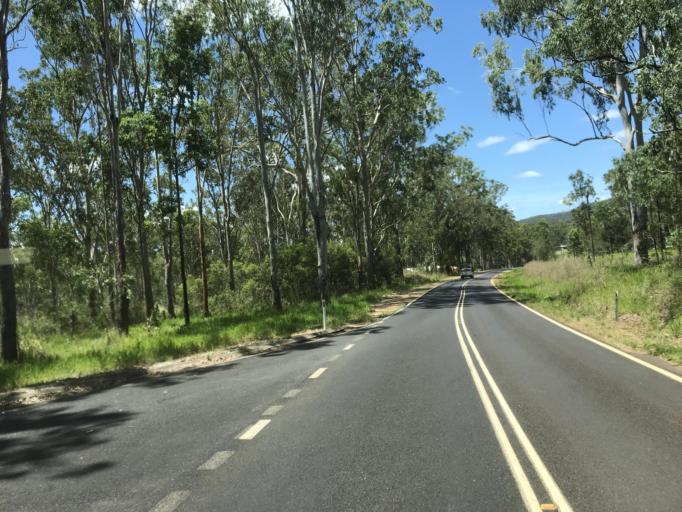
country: AU
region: Queensland
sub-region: Tablelands
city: Atherton
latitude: -17.4176
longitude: 145.3926
